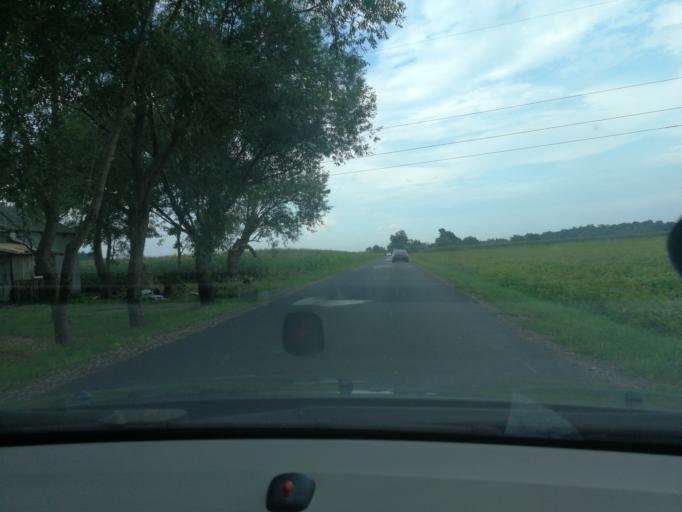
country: PL
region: Masovian Voivodeship
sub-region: Powiat grodziski
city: Grodzisk Mazowiecki
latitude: 52.1245
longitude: 20.5829
